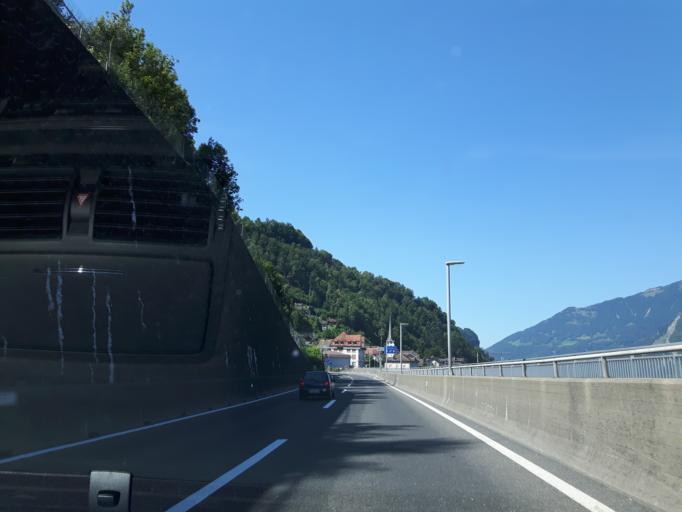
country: CH
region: Saint Gallen
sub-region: Wahlkreis See-Gaster
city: Amden
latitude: 47.1166
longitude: 9.1782
